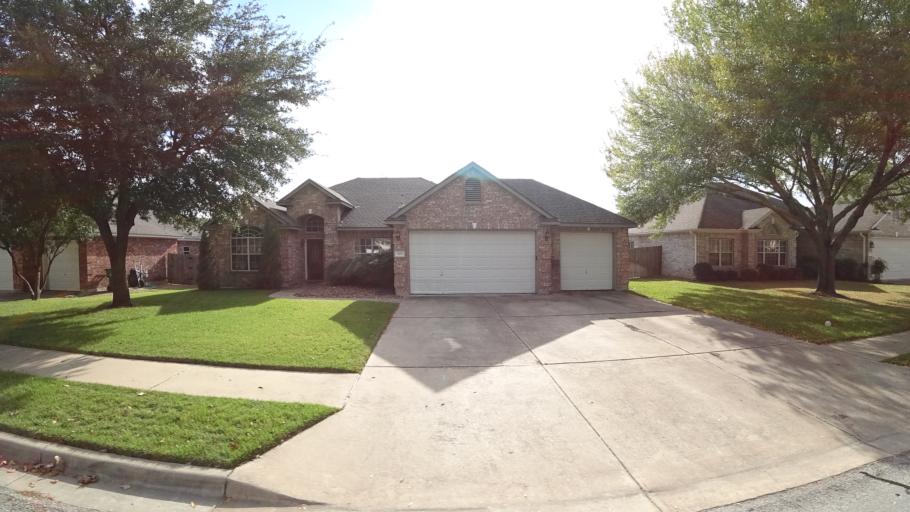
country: US
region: Texas
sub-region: Travis County
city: Pflugerville
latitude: 30.4383
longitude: -97.6285
